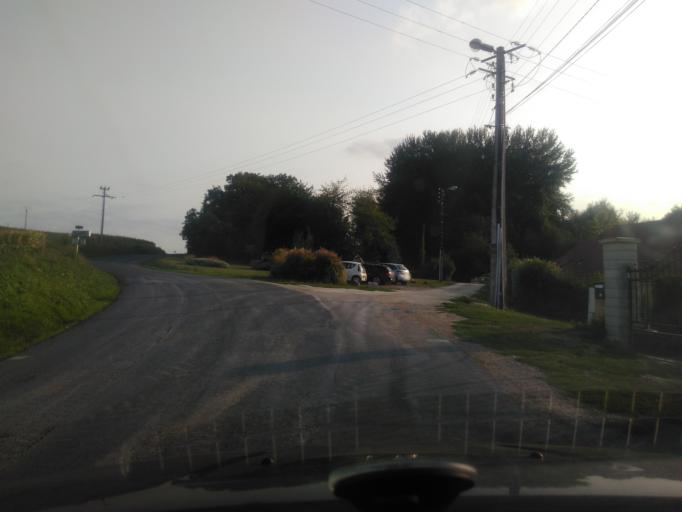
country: FR
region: Champagne-Ardenne
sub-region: Departement de la Marne
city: Fismes
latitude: 49.2656
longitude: 3.6979
